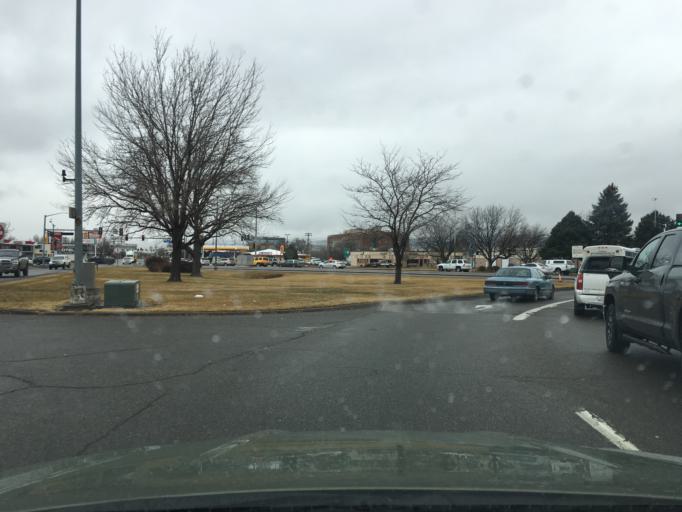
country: US
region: Colorado
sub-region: Mesa County
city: Grand Junction
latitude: 39.0715
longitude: -108.5709
